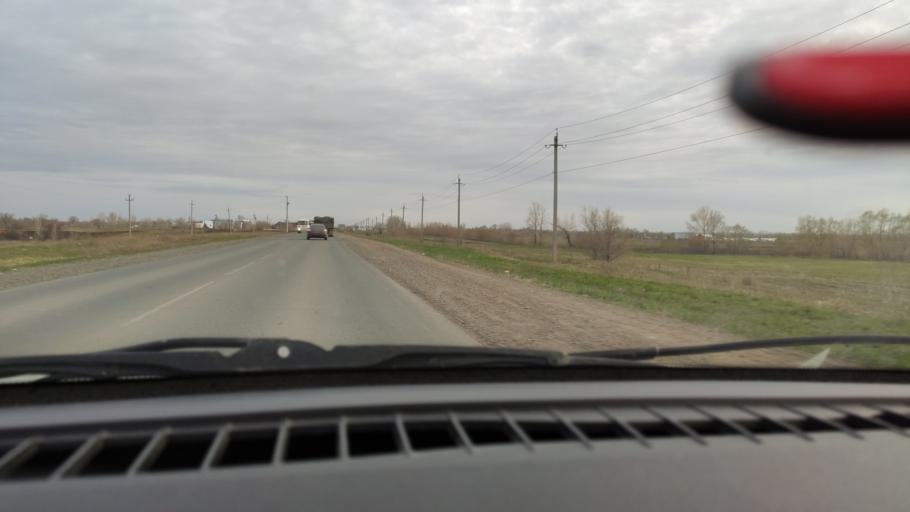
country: RU
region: Orenburg
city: Tatarskaya Kargala
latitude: 51.9091
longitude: 55.1725
